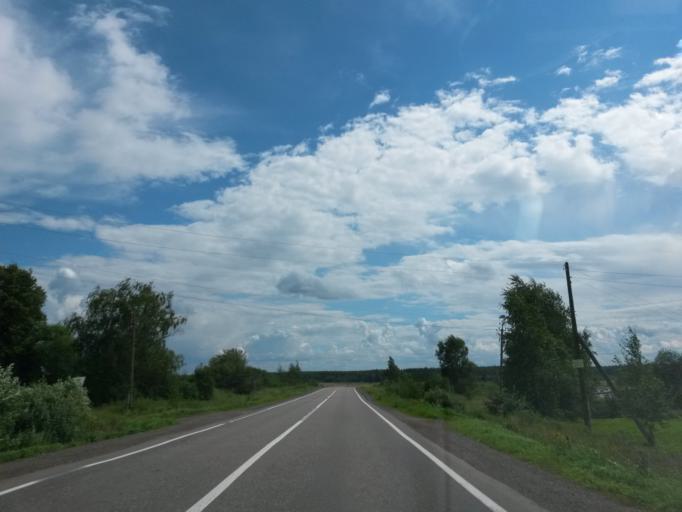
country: RU
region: Jaroslavl
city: Gavrilov-Yam
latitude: 57.3053
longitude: 39.9423
